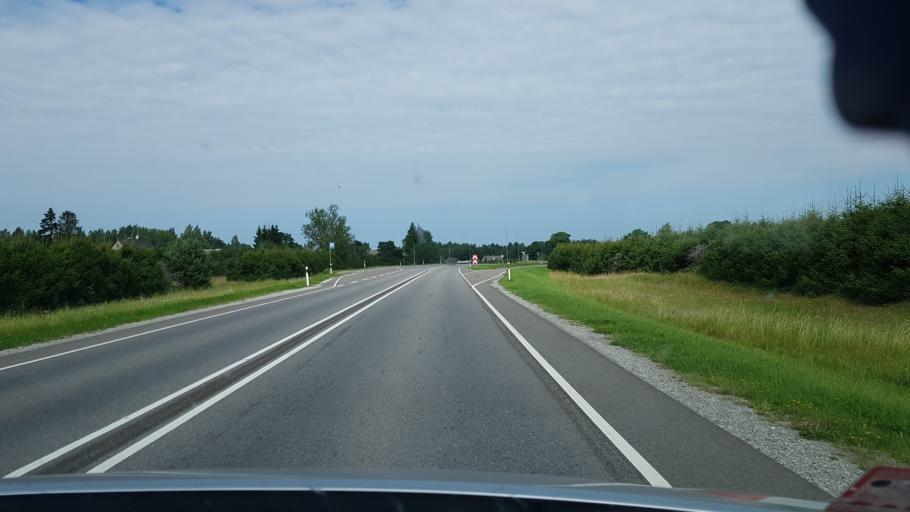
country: EE
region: Harju
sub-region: Saku vald
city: Saku
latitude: 59.3056
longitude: 24.7442
